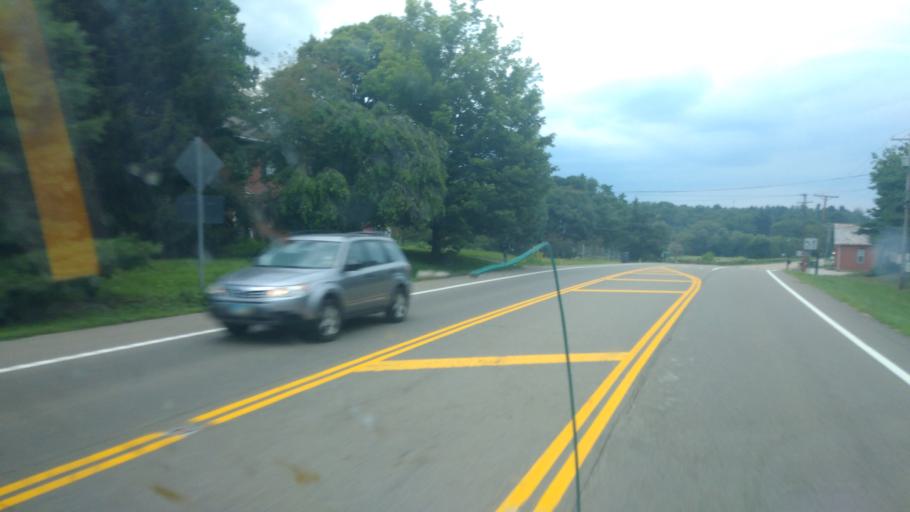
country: US
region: Ohio
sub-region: Licking County
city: Granville South
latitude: 40.0469
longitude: -82.5237
